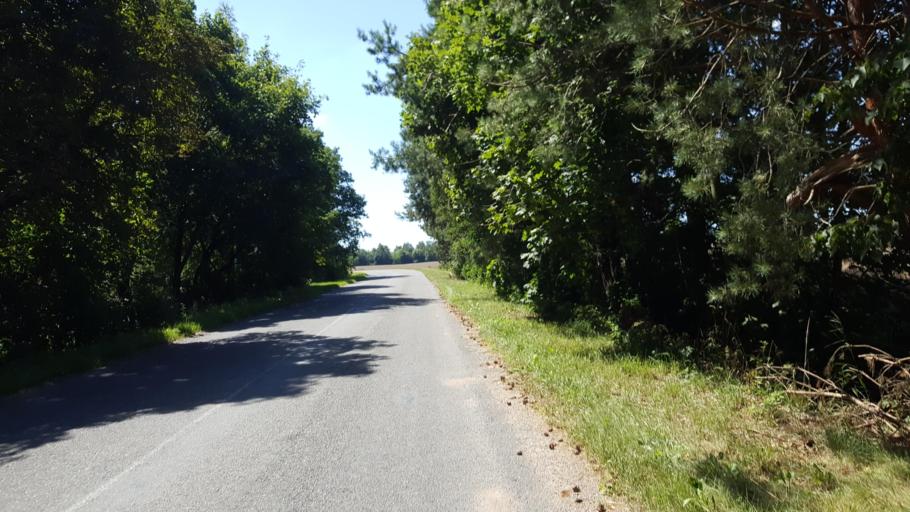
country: BY
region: Brest
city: Charnawchytsy
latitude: 52.3160
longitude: 23.6090
